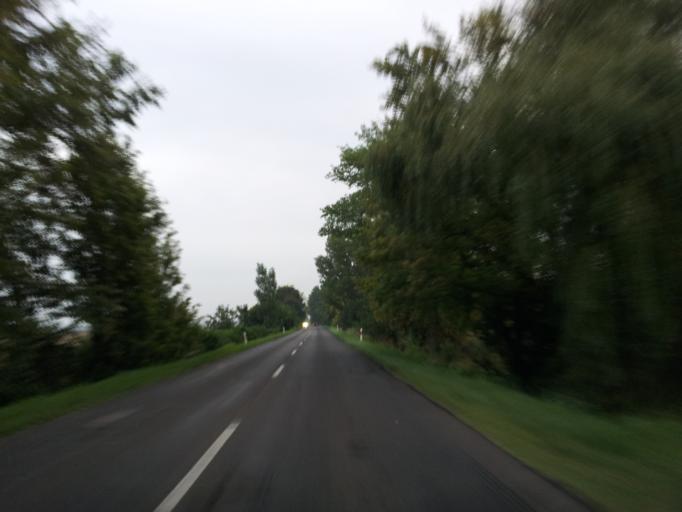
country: HU
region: Tolna
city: Tolna
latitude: 46.4366
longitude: 18.8066
